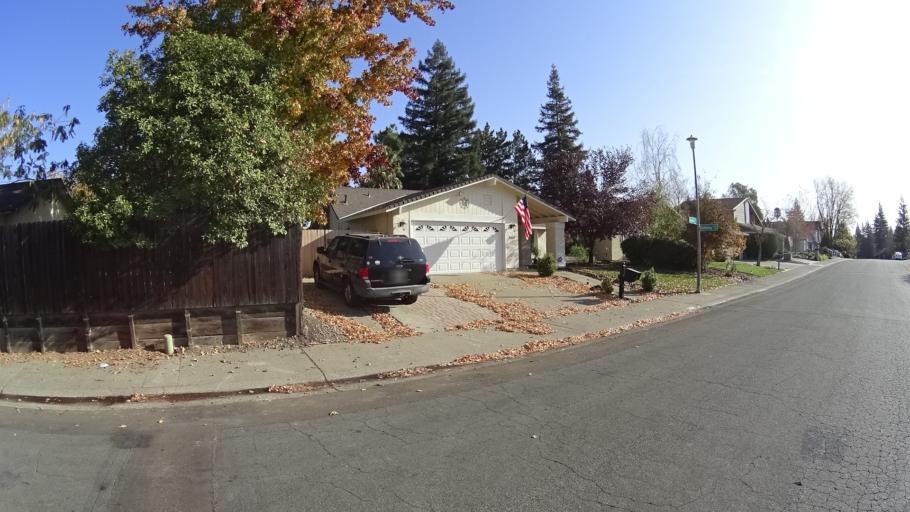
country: US
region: California
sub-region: Sacramento County
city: Orangevale
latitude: 38.6981
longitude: -121.2472
